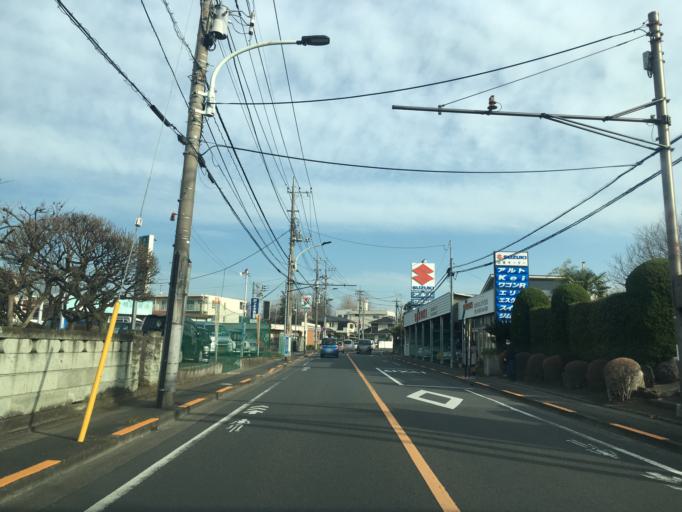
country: JP
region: Tokyo
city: Higashimurayama-shi
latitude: 35.7491
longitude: 139.4266
